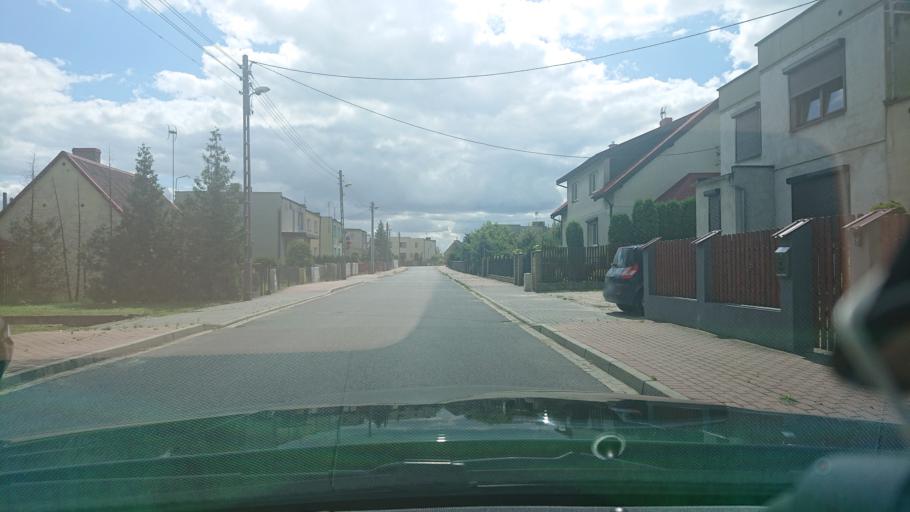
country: PL
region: Greater Poland Voivodeship
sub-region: Powiat gnieznienski
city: Gniezno
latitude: 52.5351
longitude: 17.6373
